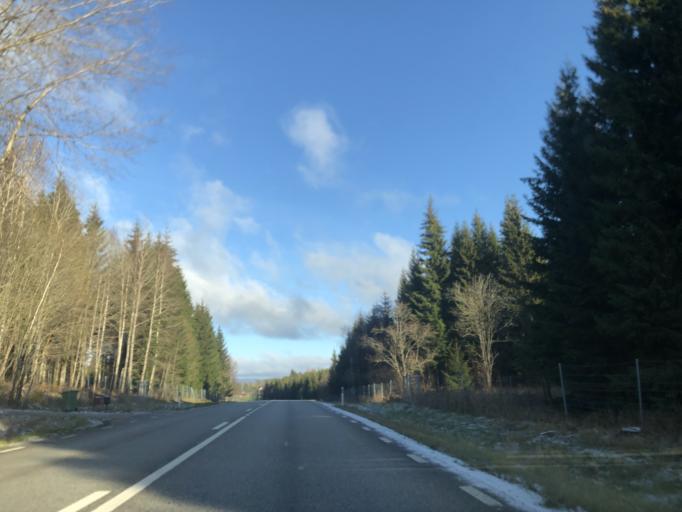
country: SE
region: Vaestra Goetaland
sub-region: Ulricehamns Kommun
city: Ulricehamn
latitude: 57.7170
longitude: 13.4341
